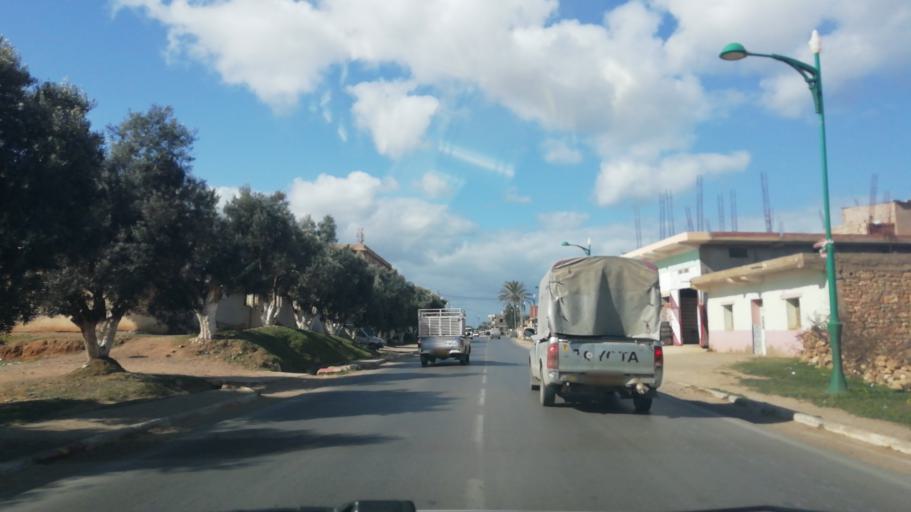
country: DZ
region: Relizane
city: Mazouna
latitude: 36.2632
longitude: 0.6177
